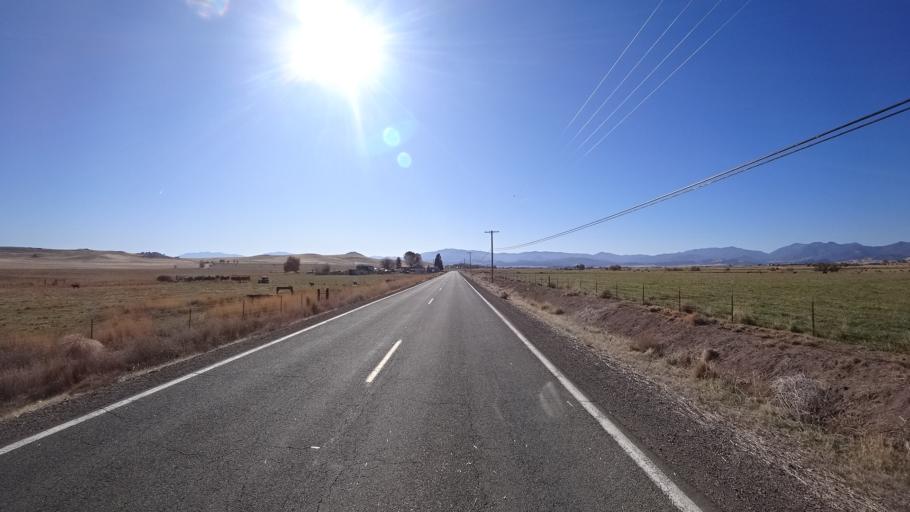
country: US
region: California
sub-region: Siskiyou County
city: Montague
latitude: 41.7550
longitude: -122.4960
